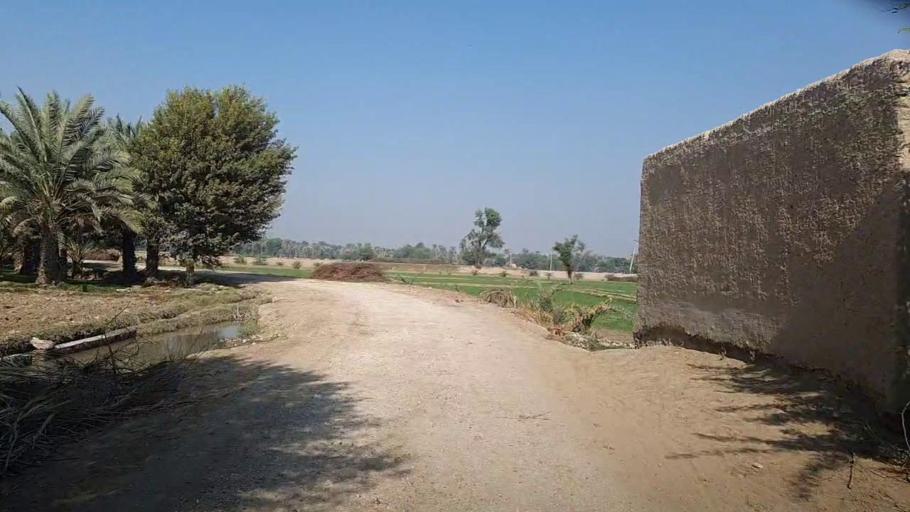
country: PK
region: Sindh
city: Bozdar
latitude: 27.1884
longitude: 68.6119
